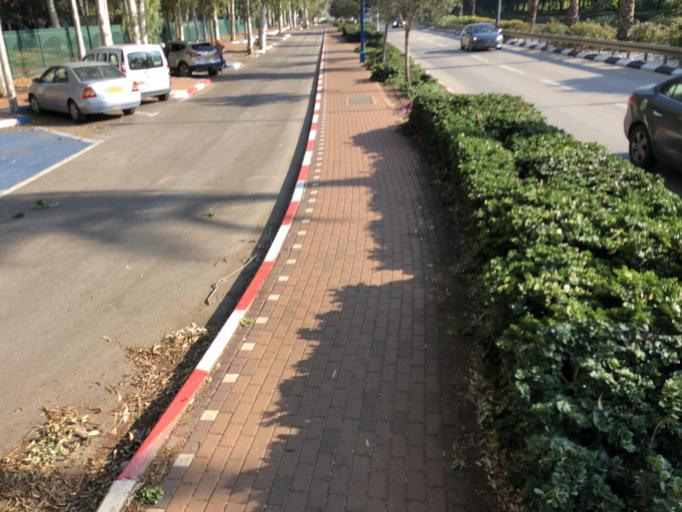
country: IL
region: Northern District
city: `Akko
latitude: 32.9231
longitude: 35.0887
